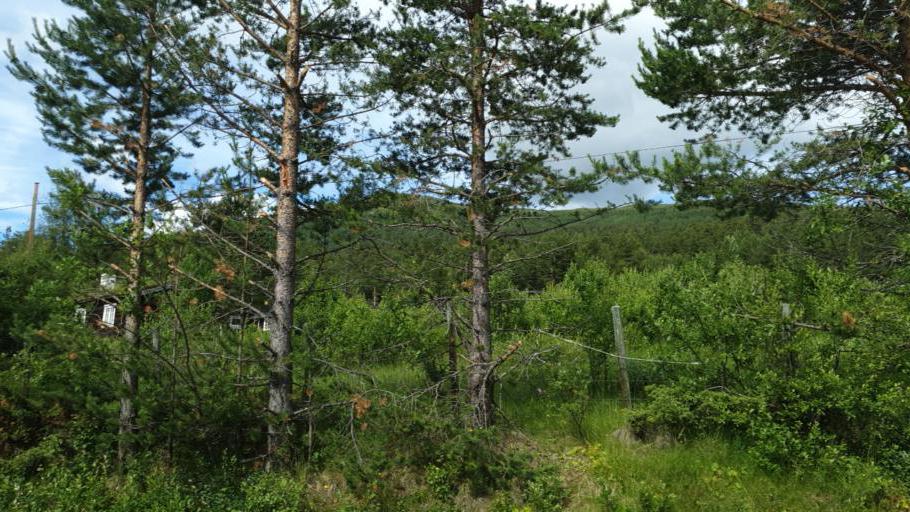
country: NO
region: Oppland
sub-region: Vaga
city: Vagamo
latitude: 61.7312
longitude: 9.0825
